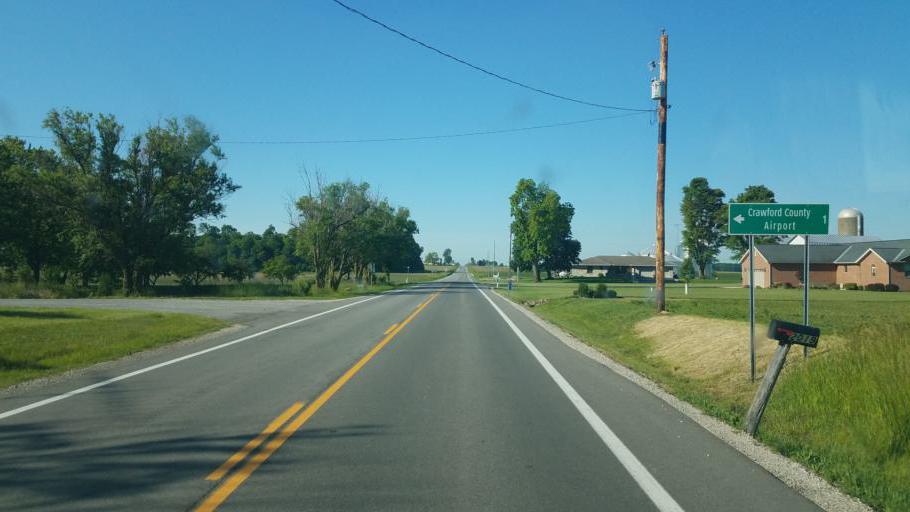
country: US
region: Ohio
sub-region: Crawford County
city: Bucyrus
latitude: 40.7768
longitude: -82.9825
